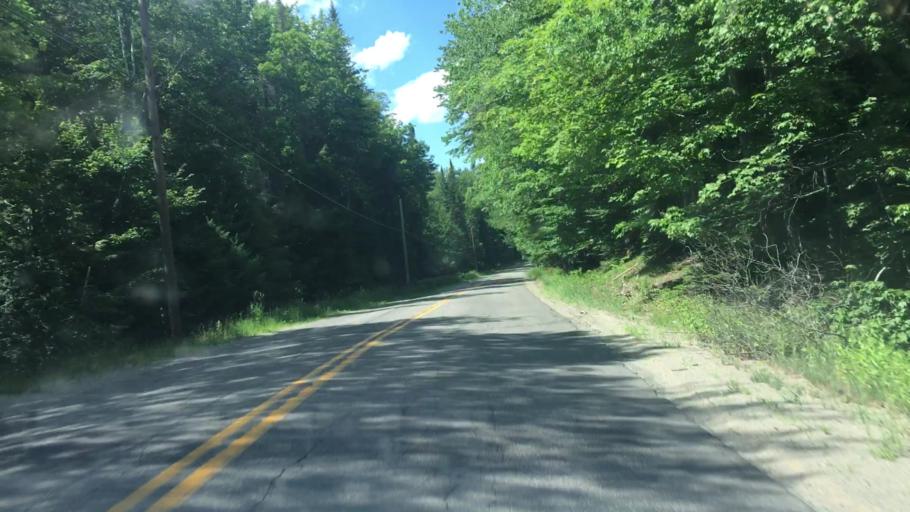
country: US
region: Maine
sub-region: Franklin County
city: Chesterville
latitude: 44.5719
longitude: -70.0891
